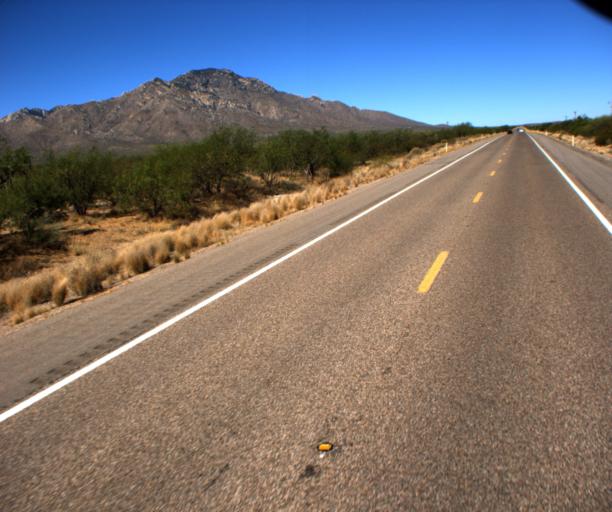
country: US
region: Arizona
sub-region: Pima County
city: Three Points
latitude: 32.0409
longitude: -111.4592
